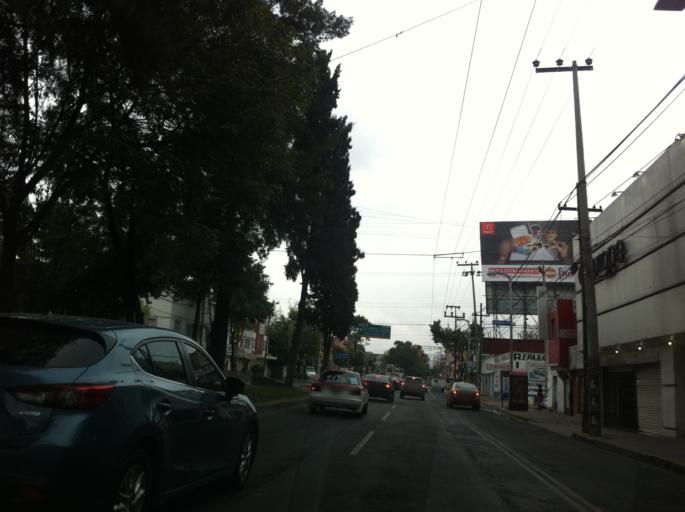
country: MX
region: Mexico City
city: Miguel Hidalgo
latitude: 19.4469
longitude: -99.1825
